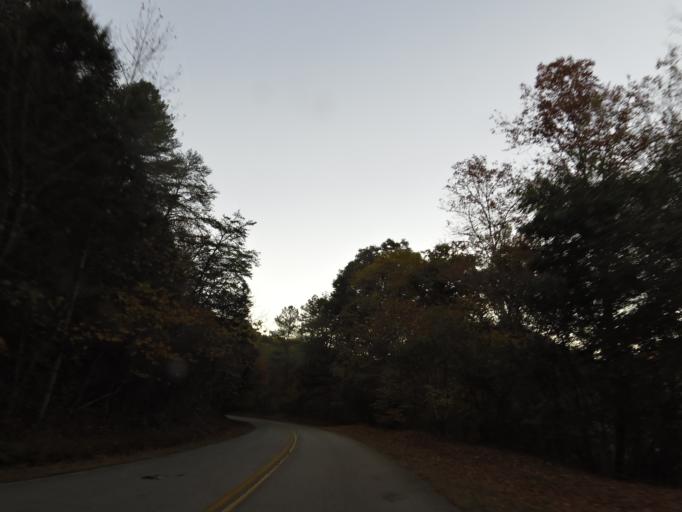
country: US
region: Tennessee
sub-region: Blount County
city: Maryville
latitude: 35.5670
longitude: -84.0029
